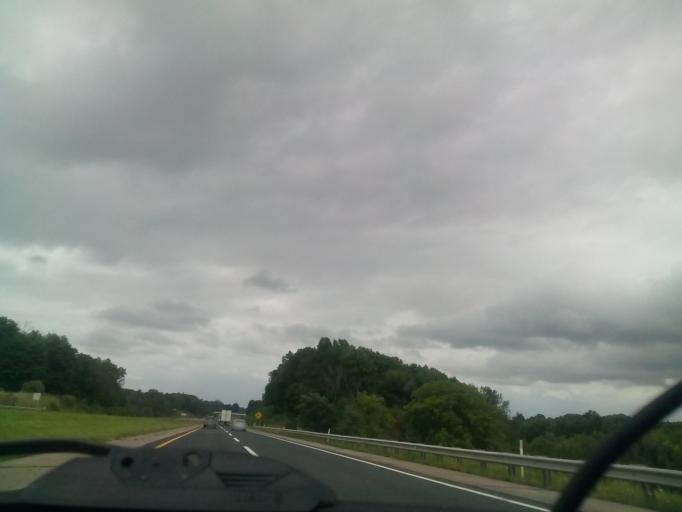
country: US
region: Indiana
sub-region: Steuben County
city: Fremont
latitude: 41.6455
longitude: -84.8394
